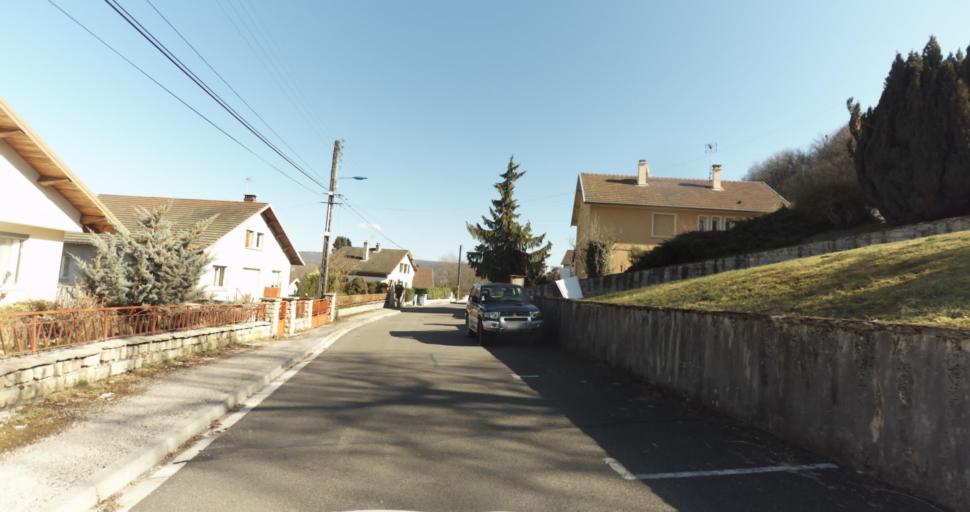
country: FR
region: Franche-Comte
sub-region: Departement du Jura
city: Montmorot
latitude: 46.6721
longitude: 5.5341
